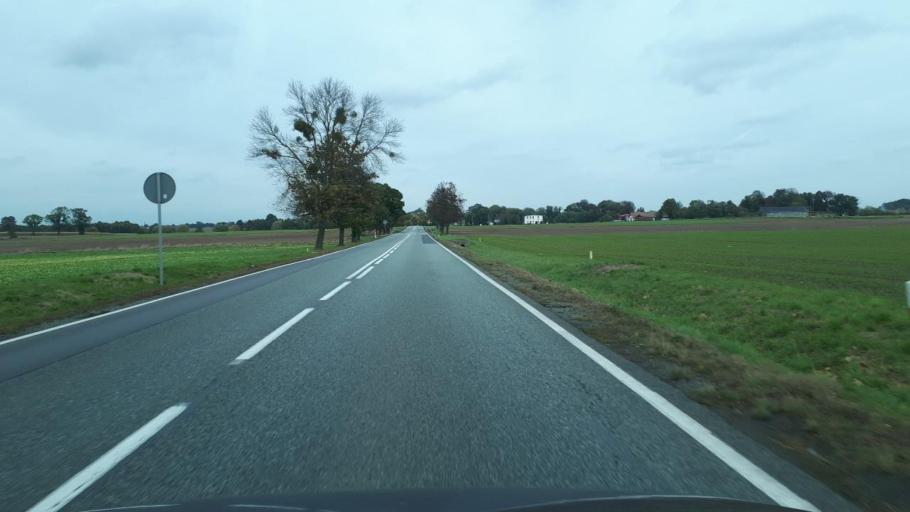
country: PL
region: Opole Voivodeship
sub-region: Powiat kluczborski
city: Byczyna
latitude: 51.0560
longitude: 18.1981
